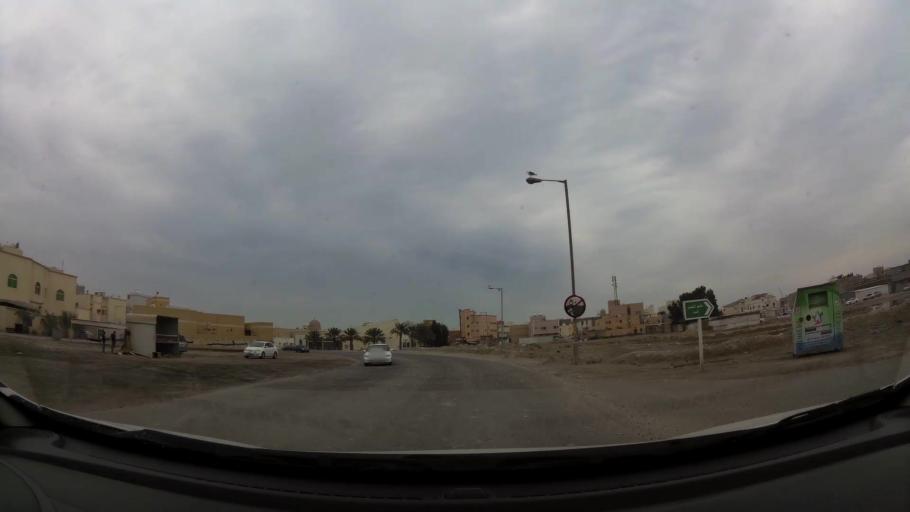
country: BH
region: Northern
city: Sitrah
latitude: 26.1632
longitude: 50.6232
